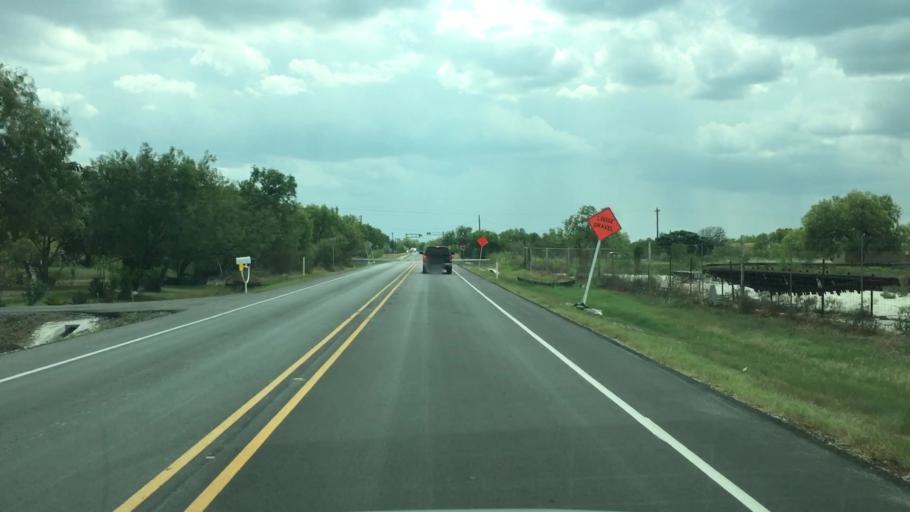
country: US
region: Texas
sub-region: Live Oak County
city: Three Rivers
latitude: 28.6371
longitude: -98.2739
